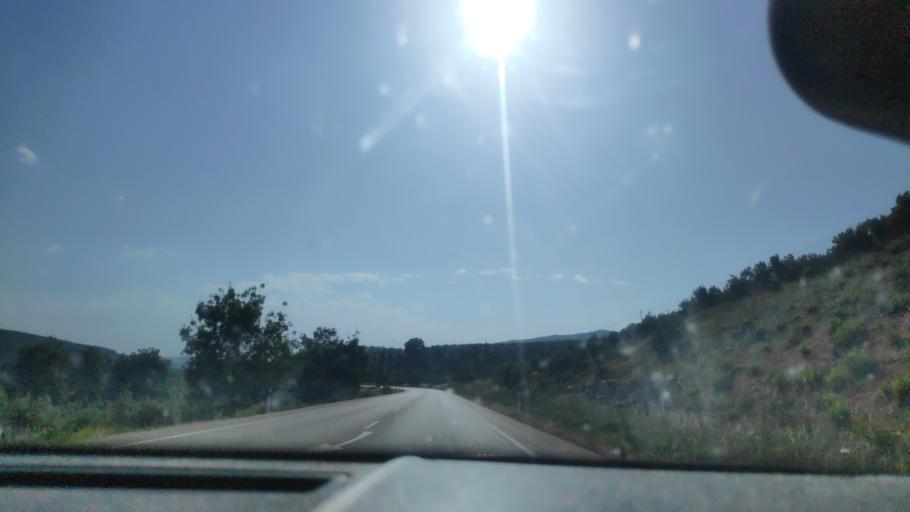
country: ES
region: Andalusia
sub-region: Provincia de Granada
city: Benalua de las Villas
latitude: 37.4391
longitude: -3.6571
